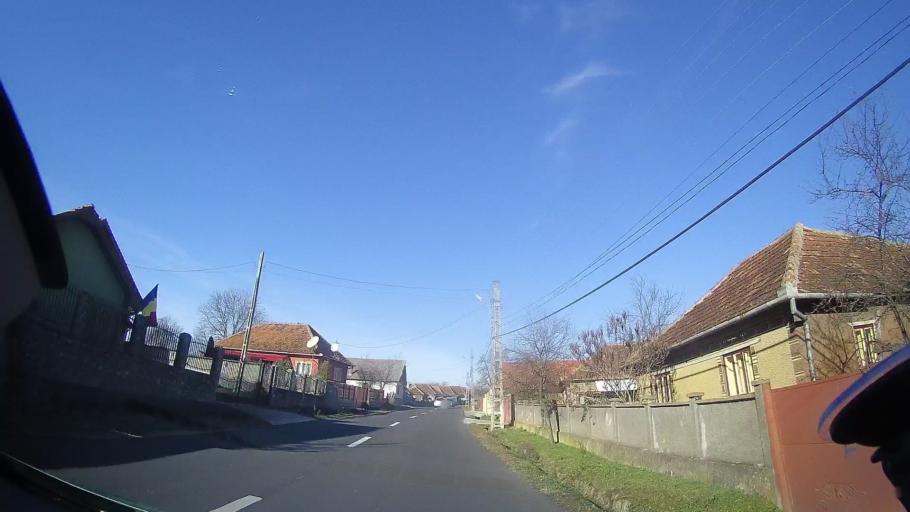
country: RO
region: Bihor
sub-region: Comuna Bratca
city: Beznea
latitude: 46.9668
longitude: 22.6153
